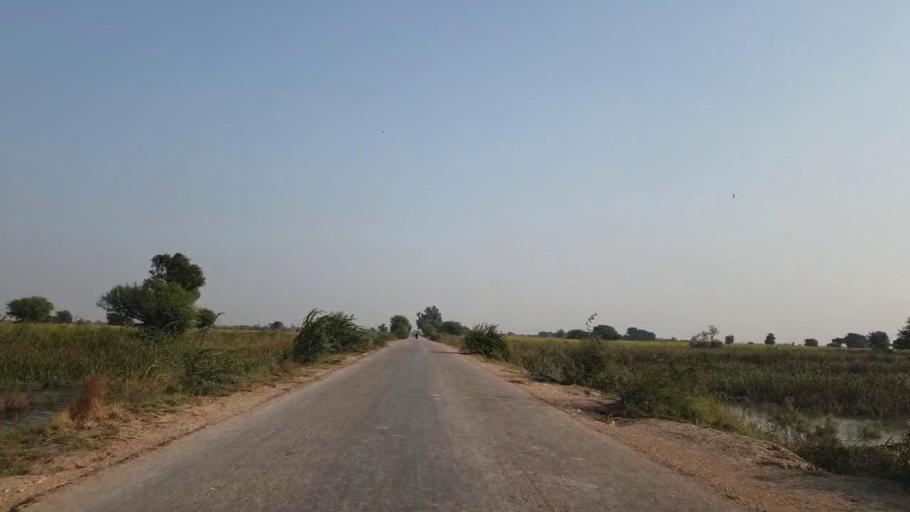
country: PK
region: Sindh
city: Bulri
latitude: 24.9773
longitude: 68.3964
